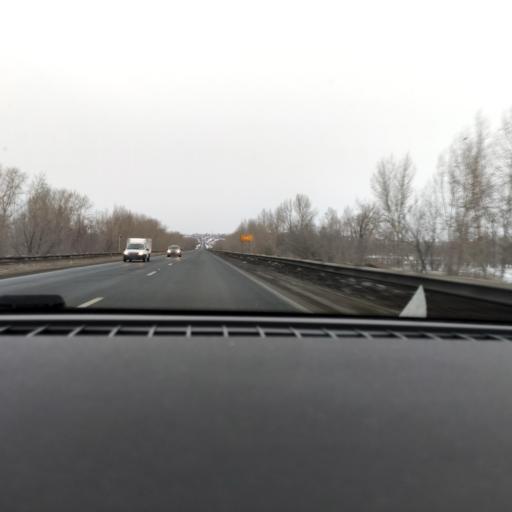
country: RU
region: Samara
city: Smyshlyayevka
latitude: 53.2214
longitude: 50.4991
